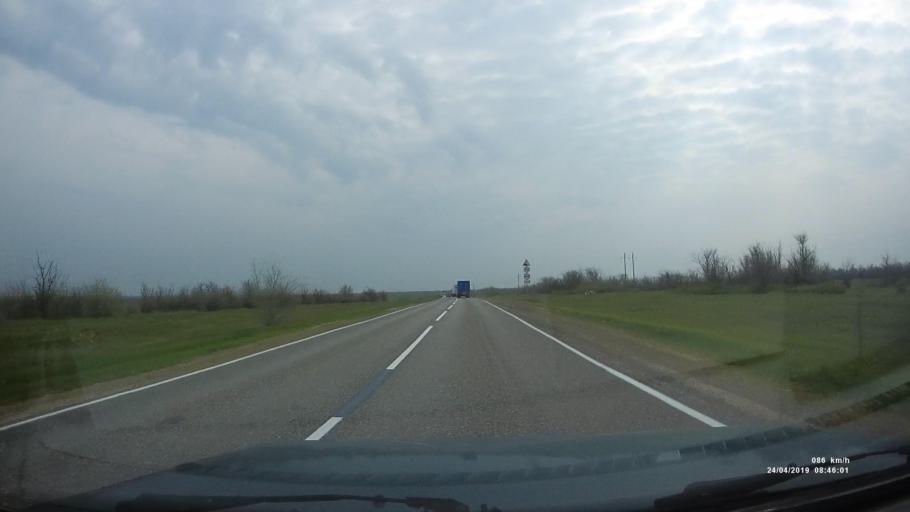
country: RU
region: Kalmykiya
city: Arshan'
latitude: 46.2366
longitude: 44.0716
